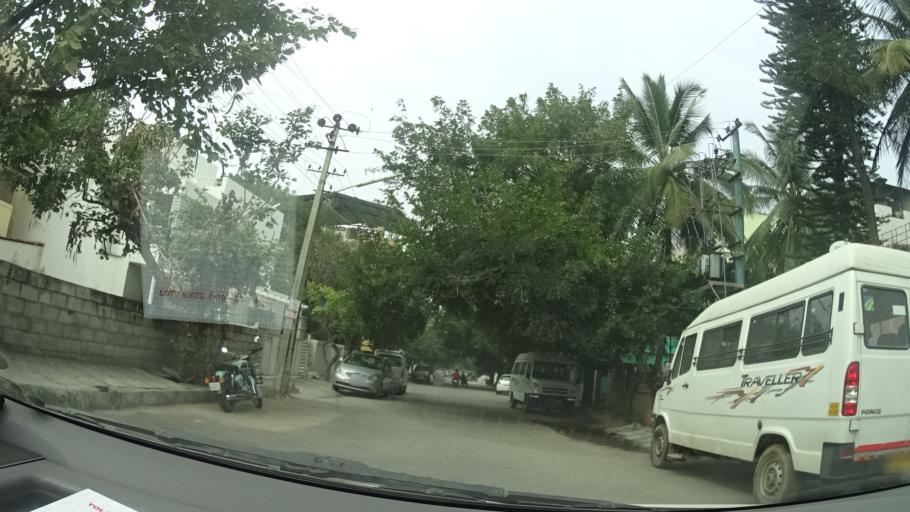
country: IN
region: Karnataka
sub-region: Bangalore Urban
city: Bangalore
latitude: 13.0254
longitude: 77.6277
